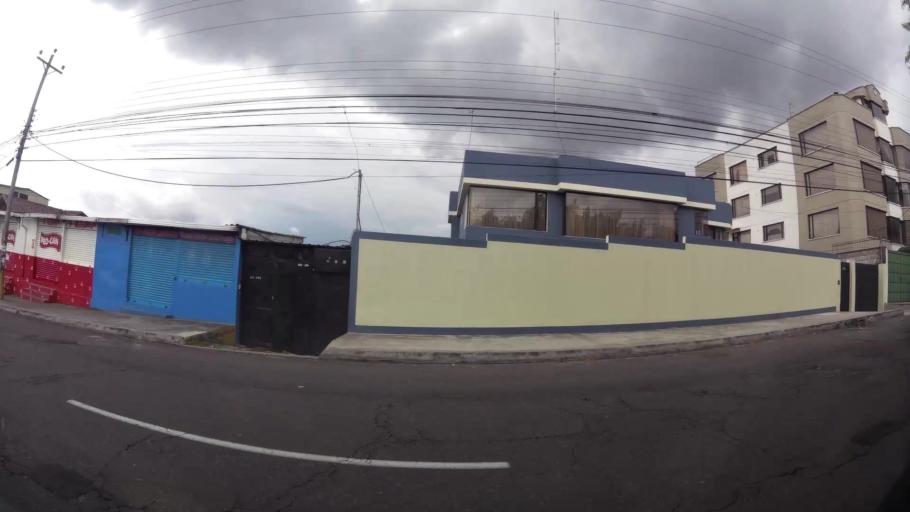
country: EC
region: Pichincha
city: Quito
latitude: -0.0847
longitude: -78.4672
